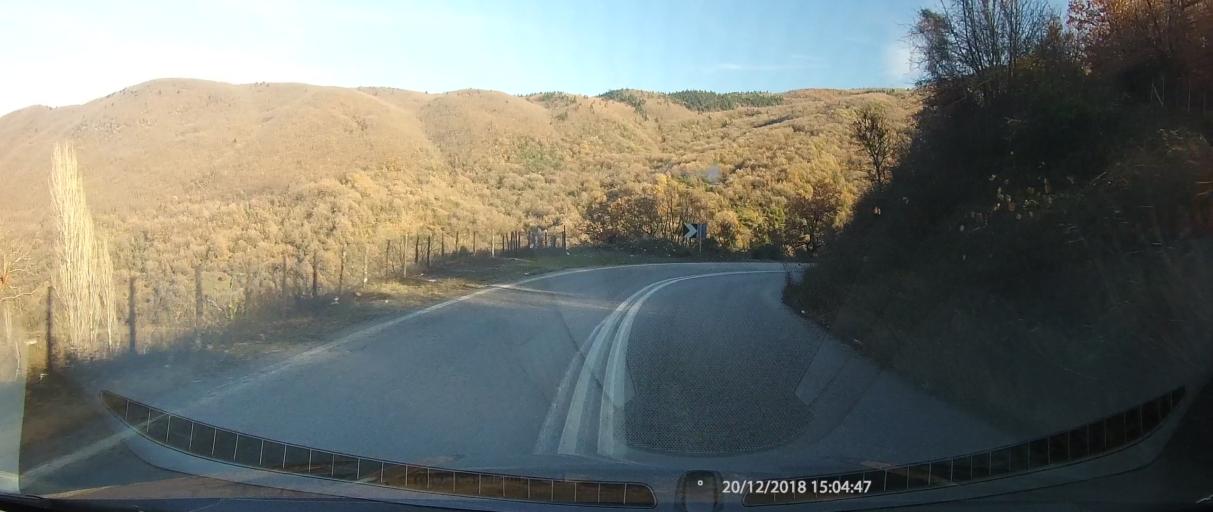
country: GR
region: Central Greece
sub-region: Nomos Evrytanias
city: Karpenisi
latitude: 38.9109
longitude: 21.9271
